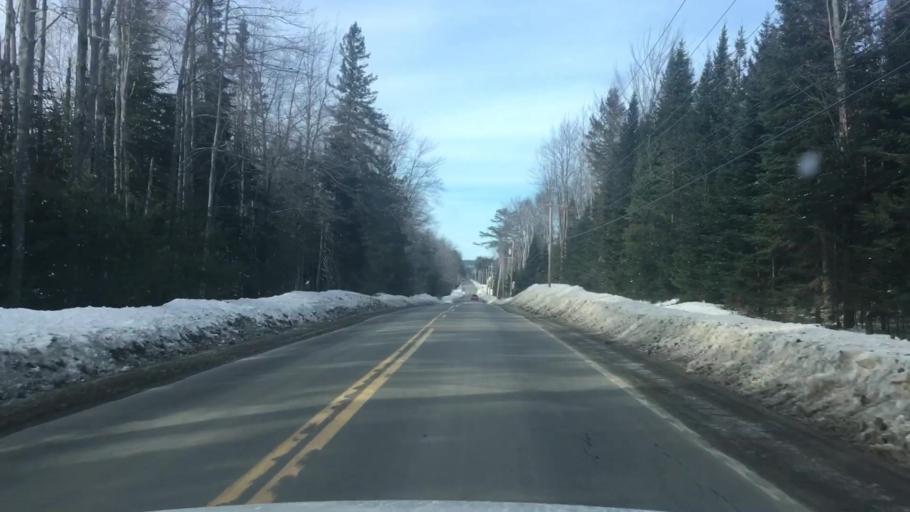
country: US
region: Maine
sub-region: Penobscot County
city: Charleston
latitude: 45.0475
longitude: -69.0292
